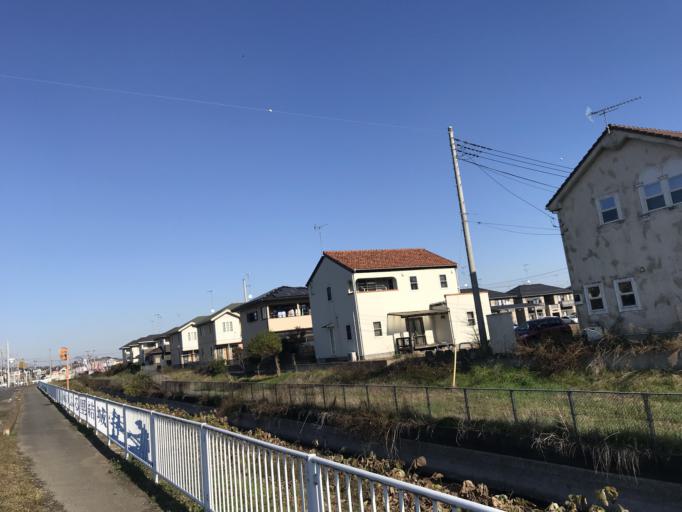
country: JP
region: Ibaraki
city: Yuki
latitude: 36.2907
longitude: 139.8624
